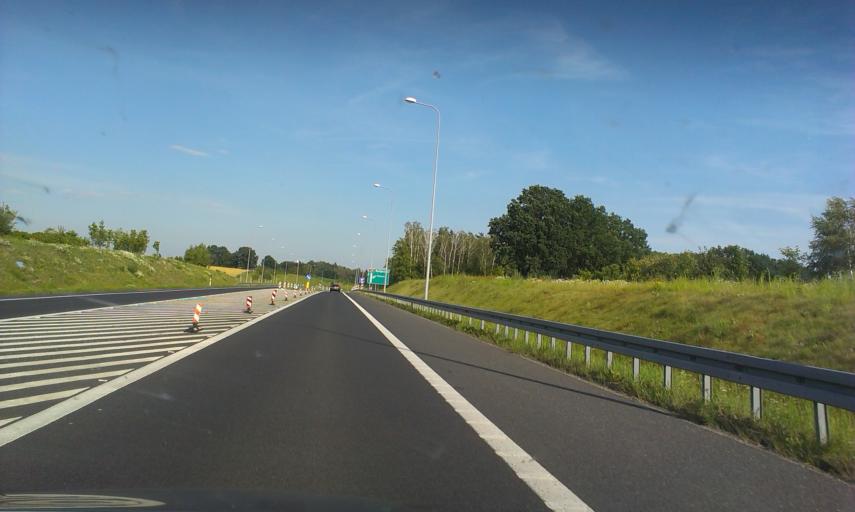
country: PL
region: Greater Poland Voivodeship
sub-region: Powiat pilski
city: Wyrzysk
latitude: 53.1603
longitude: 17.2927
